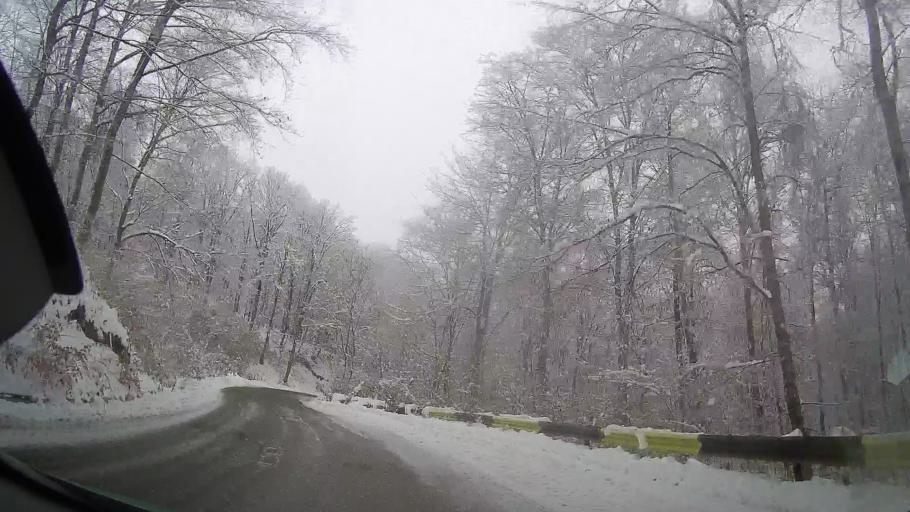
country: RO
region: Neamt
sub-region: Comuna Valea Ursului
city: Valea Ursului
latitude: 46.8468
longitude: 27.0657
